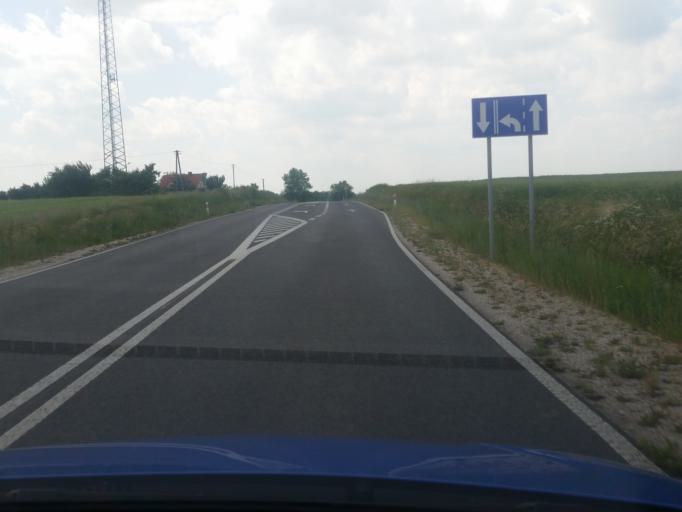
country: PL
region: Swietokrzyskie
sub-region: Powiat kazimierski
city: Czarnocin
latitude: 50.3257
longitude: 20.5656
